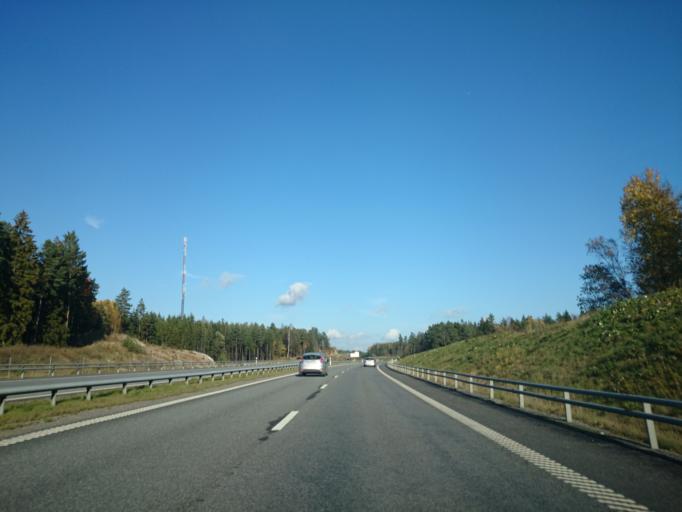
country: SE
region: Stockholm
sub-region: Haninge Kommun
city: Jordbro
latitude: 59.0741
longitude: 18.0700
